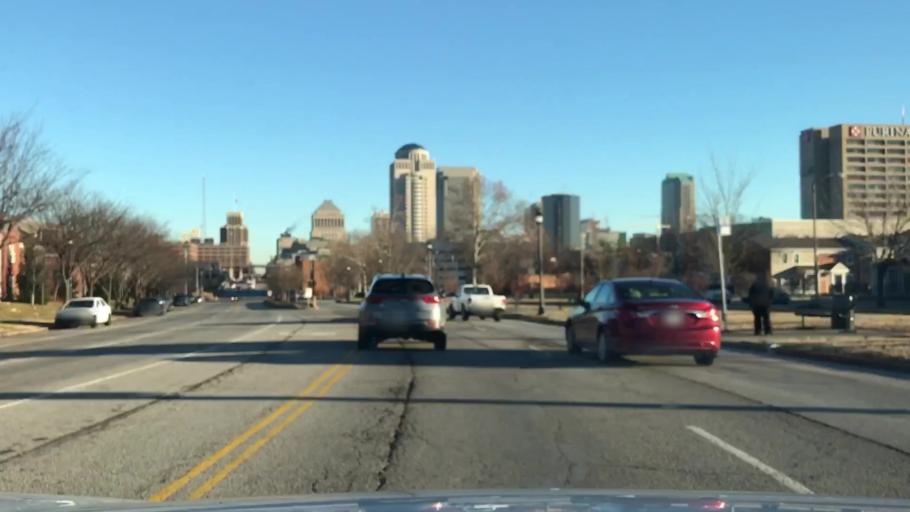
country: US
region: Missouri
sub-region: City of Saint Louis
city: St. Louis
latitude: 38.6167
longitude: -90.2024
